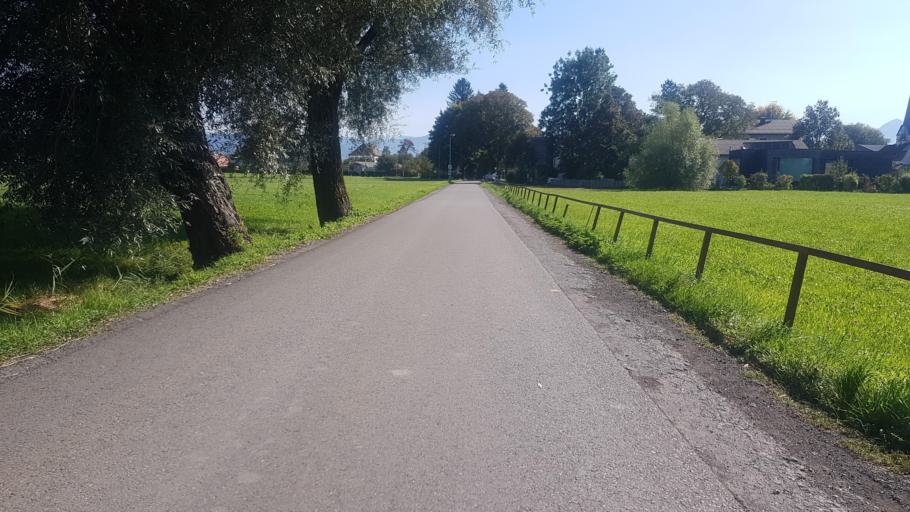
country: AT
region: Vorarlberg
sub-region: Politischer Bezirk Bregenz
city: Fussach
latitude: 47.4822
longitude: 9.6614
